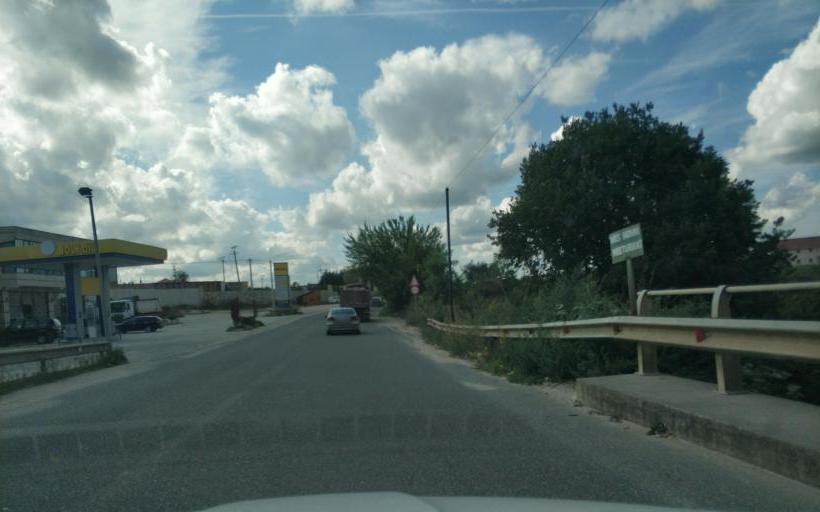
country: AL
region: Durres
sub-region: Rrethi i Krujes
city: Fushe-Kruje
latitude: 41.4769
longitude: 19.7502
